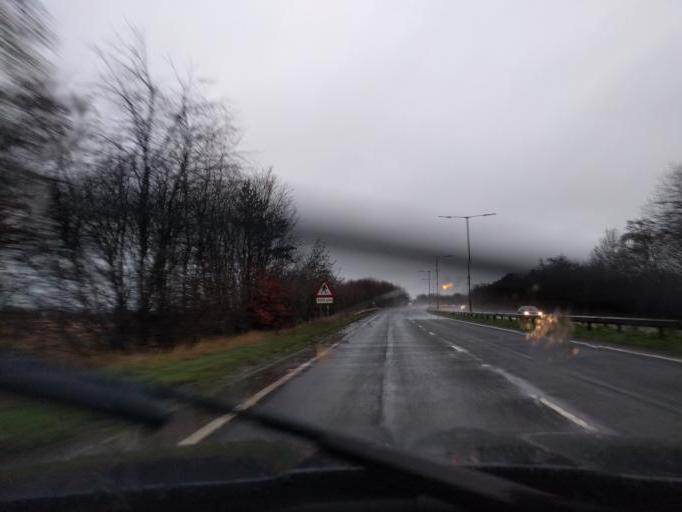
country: GB
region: England
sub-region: Northumberland
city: Newbiggin-by-the-Sea
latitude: 55.1808
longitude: -1.5336
